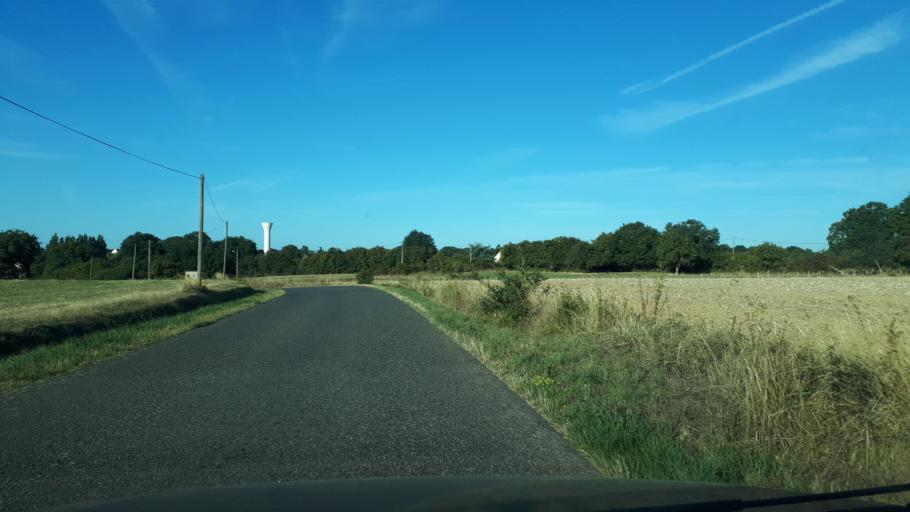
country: FR
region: Centre
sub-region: Departement du Loir-et-Cher
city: Montoire-sur-le-Loir
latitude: 47.6989
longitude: 0.9256
